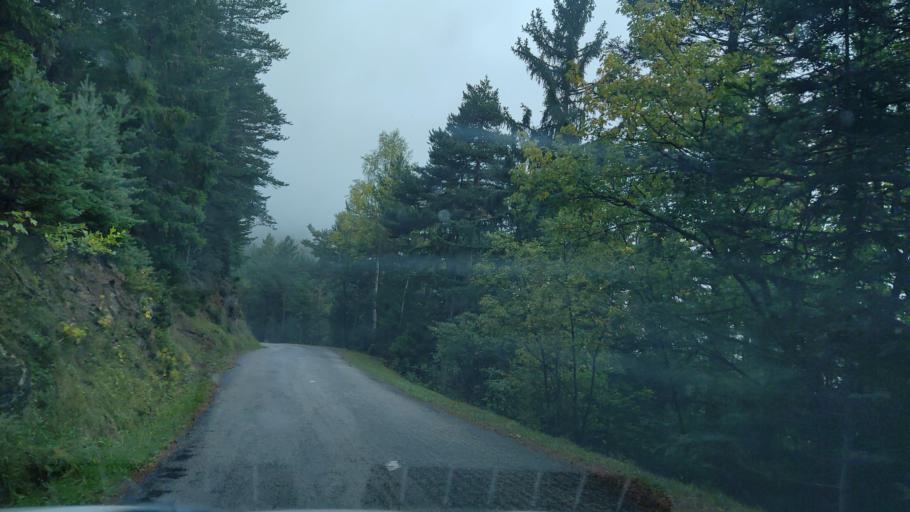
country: FR
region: Rhone-Alpes
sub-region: Departement de la Savoie
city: Modane
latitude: 45.2942
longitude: 6.8199
